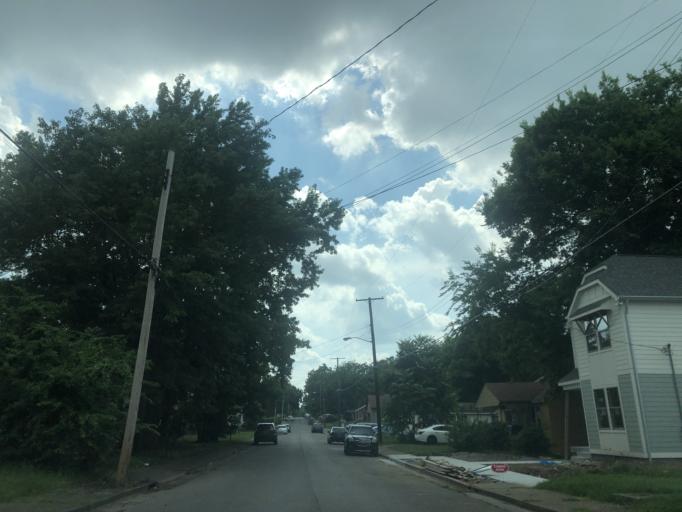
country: US
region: Tennessee
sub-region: Davidson County
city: Nashville
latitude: 36.1665
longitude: -86.8131
